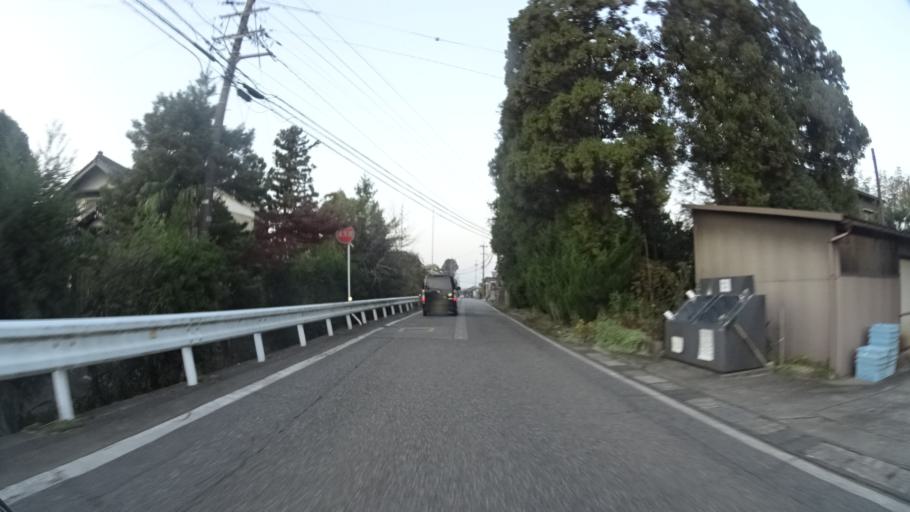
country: JP
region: Toyama
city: Kamiichi
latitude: 36.7161
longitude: 137.3682
